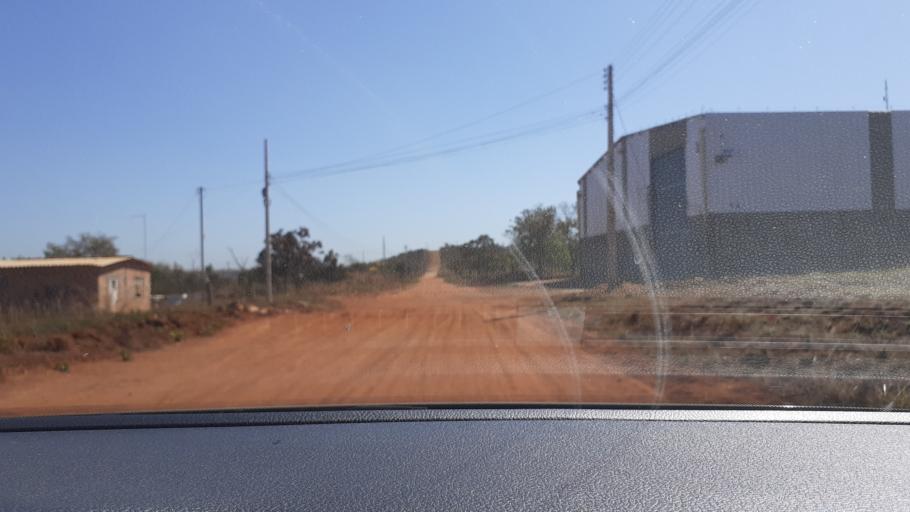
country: BR
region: Goias
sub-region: Aparecida De Goiania
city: Aparecida de Goiania
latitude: -16.8885
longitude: -49.2589
